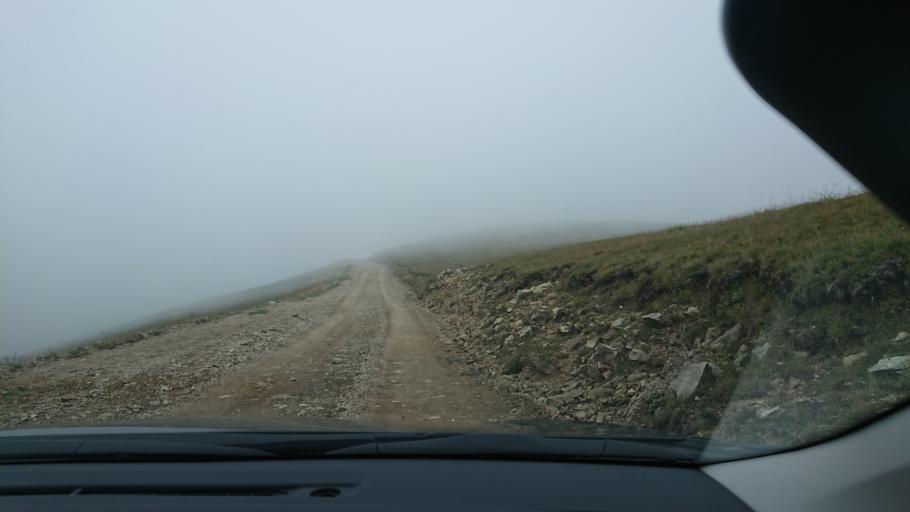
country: TR
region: Gumushane
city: Kurtun
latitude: 40.6241
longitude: 38.9931
